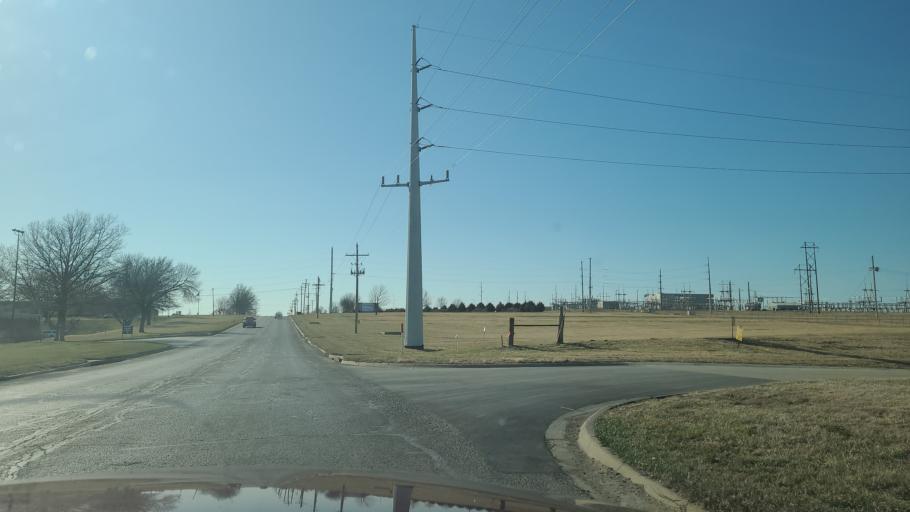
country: US
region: Kansas
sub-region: Douglas County
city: Lawrence
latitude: 39.0007
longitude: -95.2671
